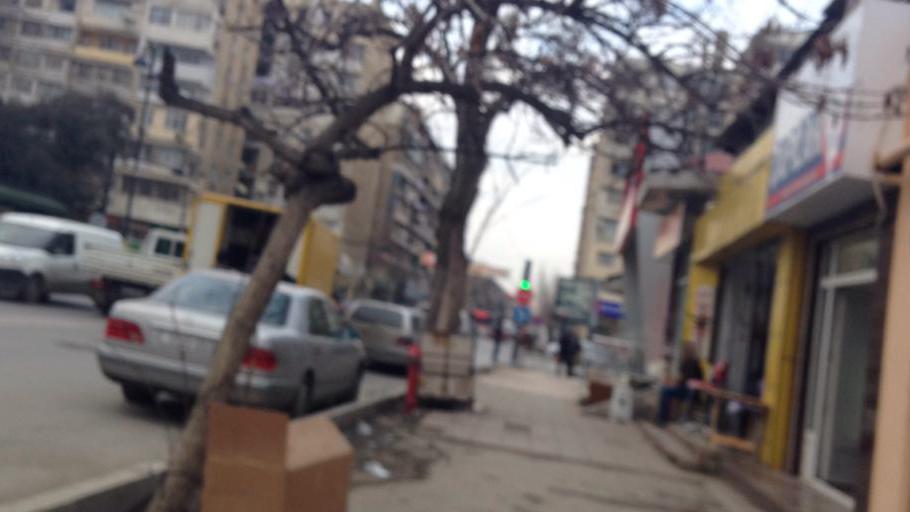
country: AZ
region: Baki
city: Bilajari
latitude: 40.3997
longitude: 49.8378
